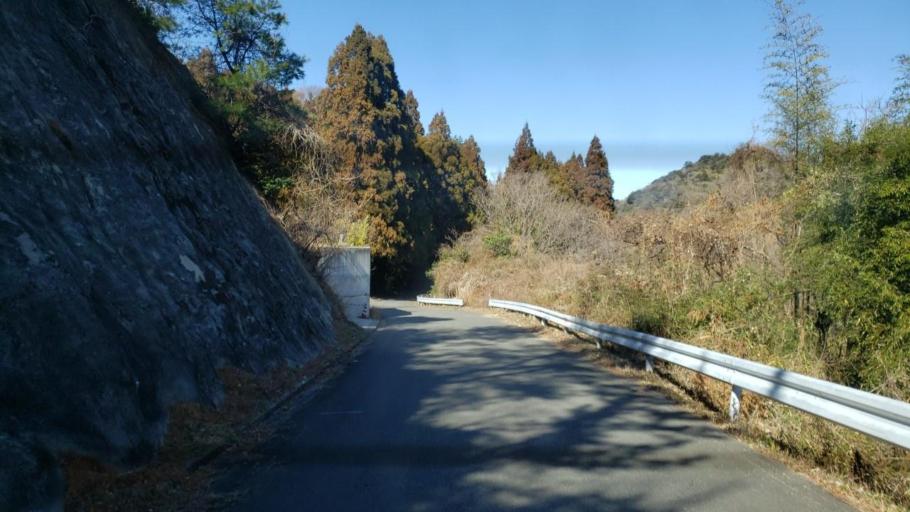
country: JP
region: Tokushima
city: Narutocho-mitsuishi
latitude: 34.1999
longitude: 134.5539
